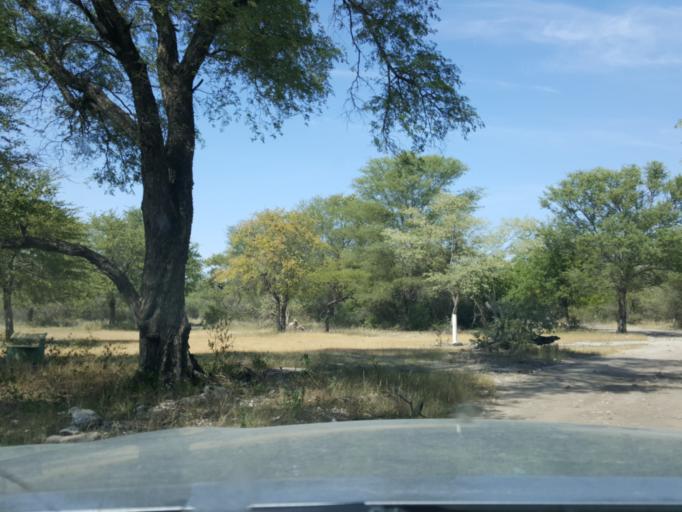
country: BW
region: North West
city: Shakawe
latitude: -18.7596
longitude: 21.7379
